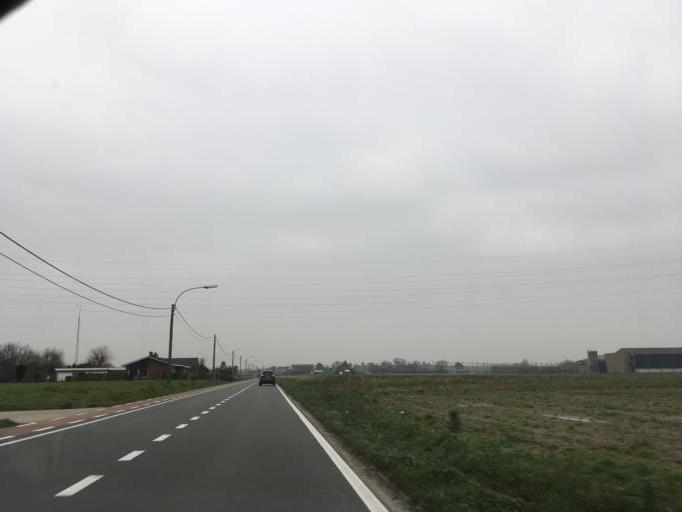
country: BE
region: Flanders
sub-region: Provincie West-Vlaanderen
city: Ardooie
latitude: 50.9680
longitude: 3.2284
